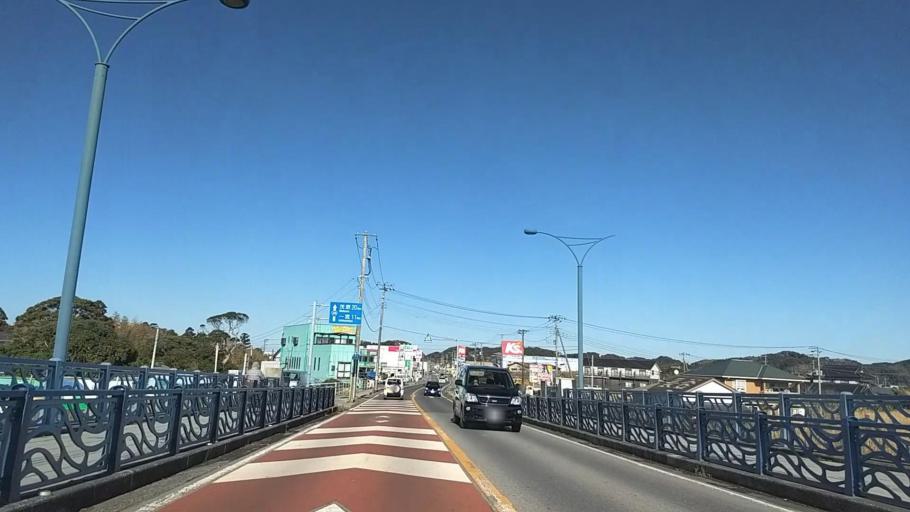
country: JP
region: Chiba
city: Ohara
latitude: 35.2987
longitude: 140.3968
